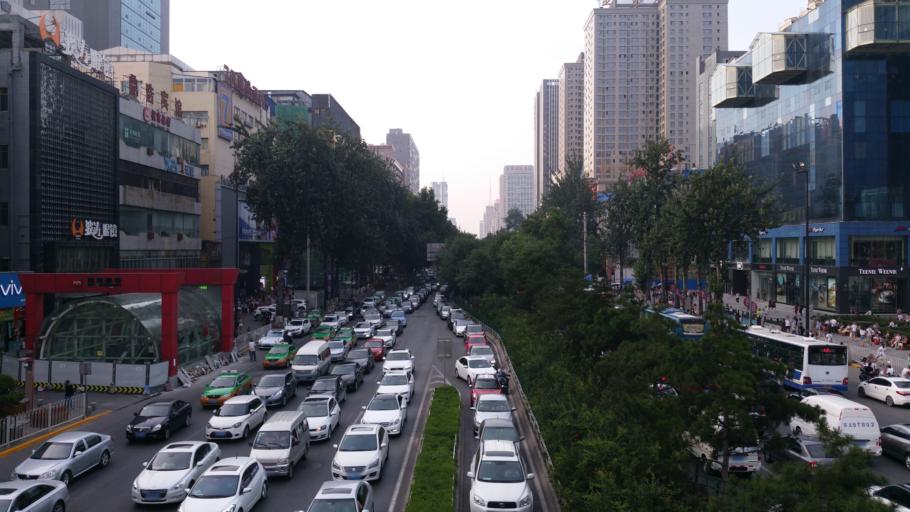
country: CN
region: Shaanxi
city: Yanta
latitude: 34.2244
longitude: 108.9424
